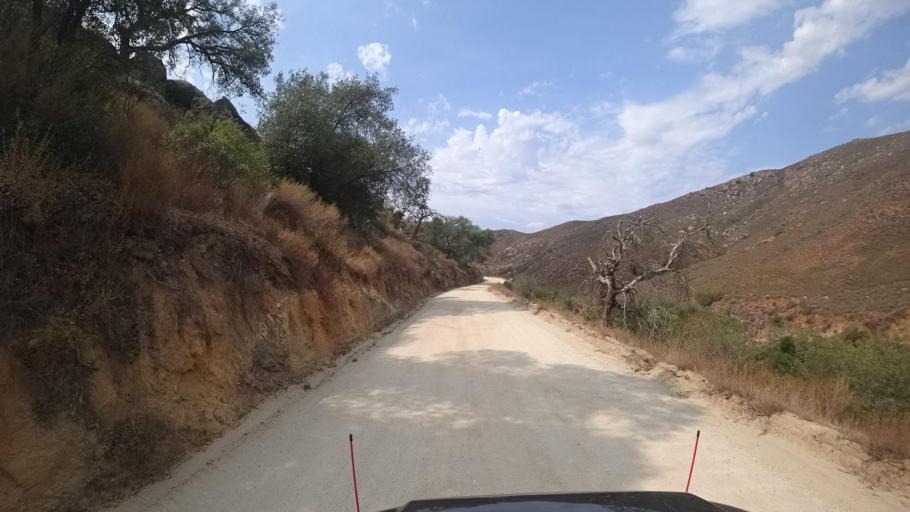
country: US
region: California
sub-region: San Diego County
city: Ramona
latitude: 33.1280
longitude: -116.8001
